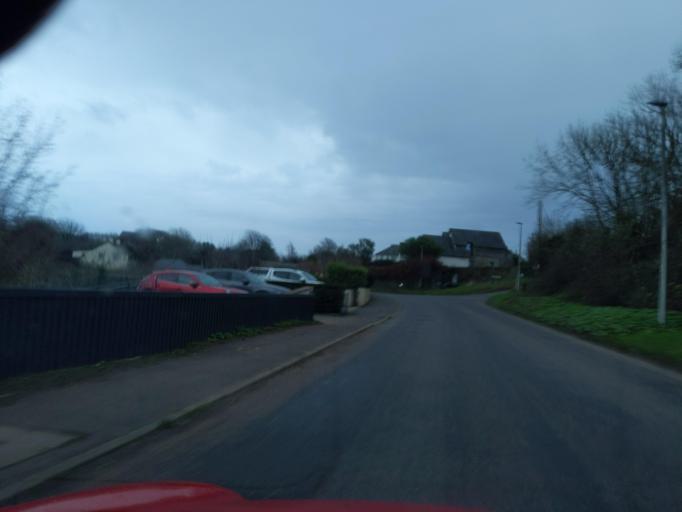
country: GB
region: England
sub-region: Devon
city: Wembury
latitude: 50.3362
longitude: -4.0724
